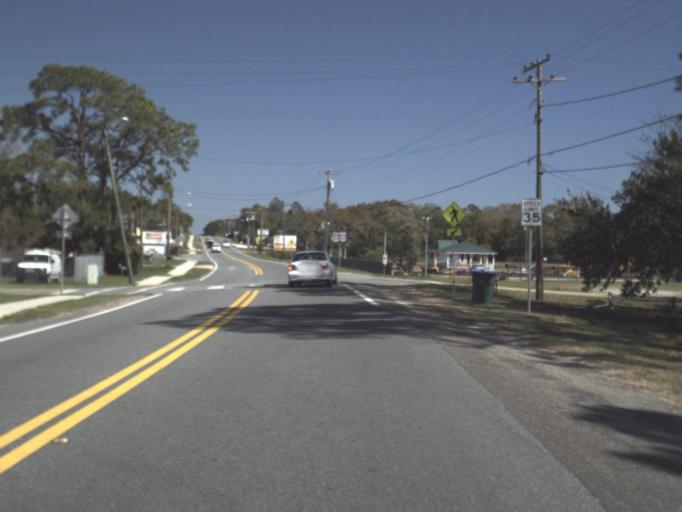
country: US
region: Florida
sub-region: Franklin County
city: Carrabelle
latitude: 29.8503
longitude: -84.6624
